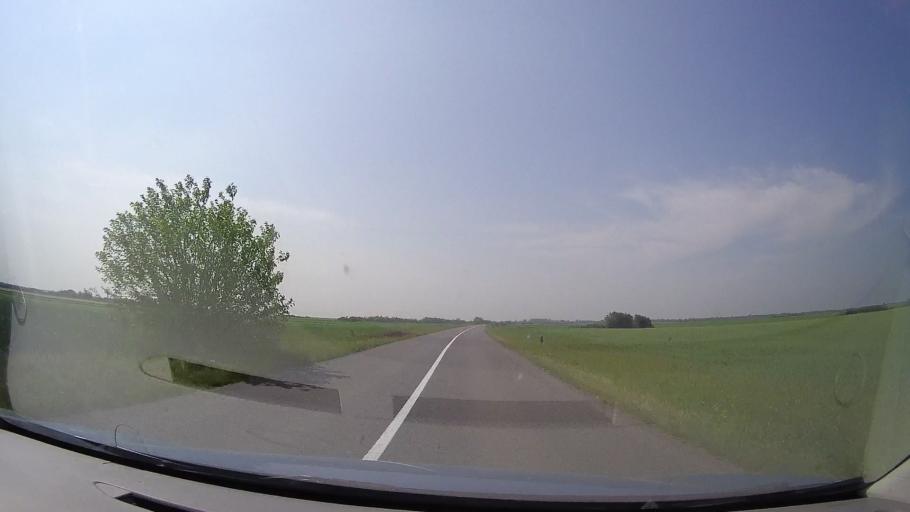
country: RS
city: Jarkovac
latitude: 45.2937
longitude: 20.7643
